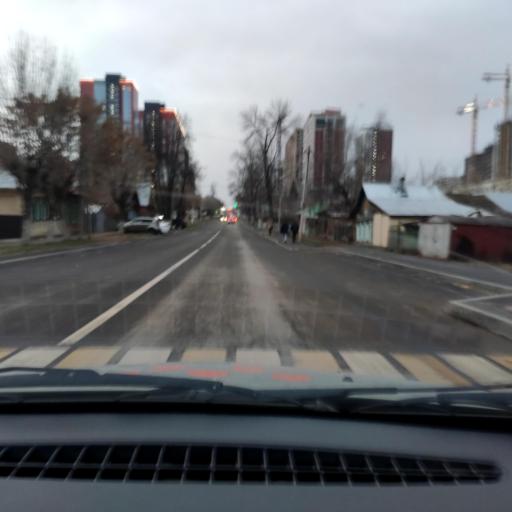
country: RU
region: Bashkortostan
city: Ufa
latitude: 54.7339
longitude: 55.9320
